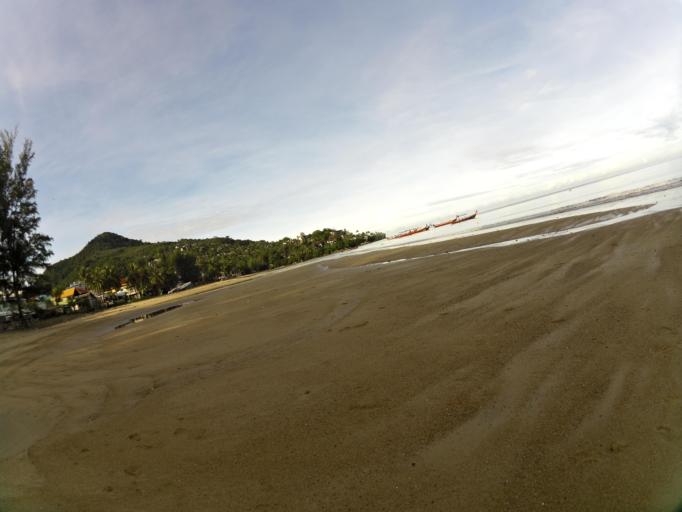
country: TH
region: Phuket
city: Patong
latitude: 7.9520
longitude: 98.2817
